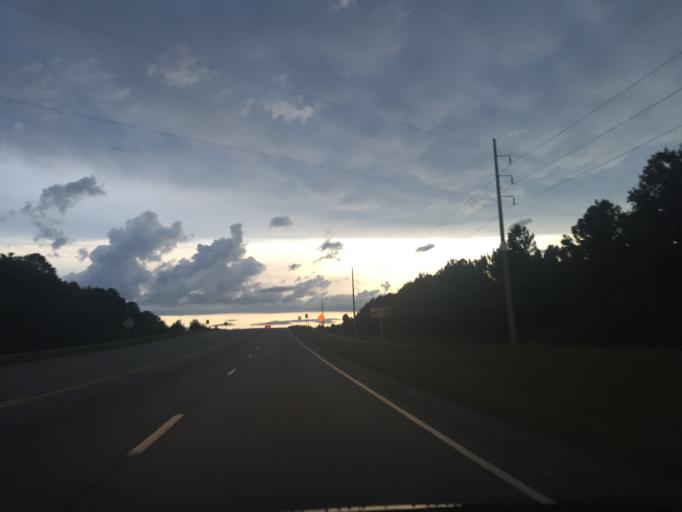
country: US
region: Georgia
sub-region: Liberty County
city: Hinesville
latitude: 31.8294
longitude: -81.5285
